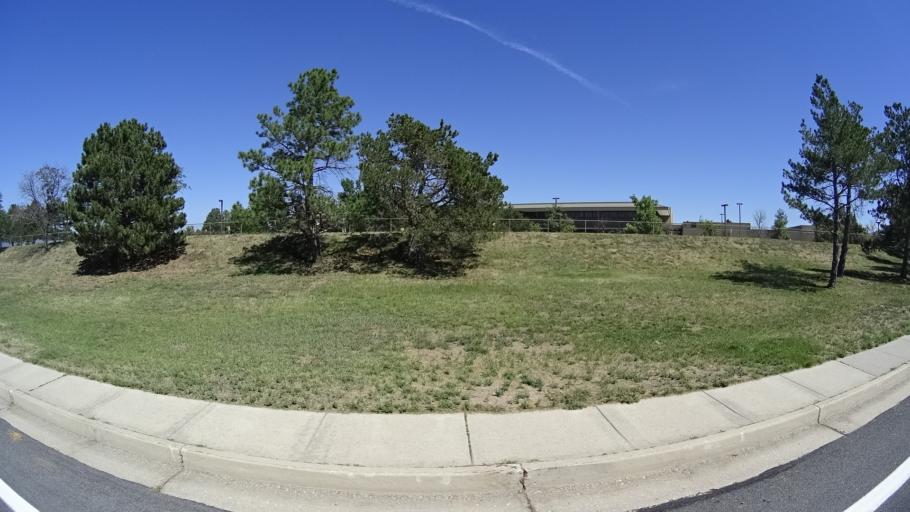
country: US
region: Colorado
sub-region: El Paso County
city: Black Forest
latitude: 38.9475
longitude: -104.7628
